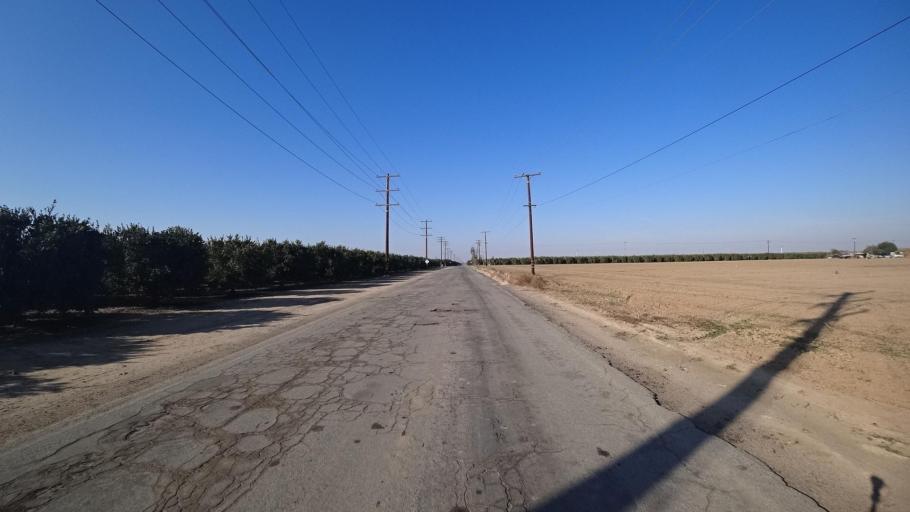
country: US
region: California
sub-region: Tulare County
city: Richgrove
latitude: 35.7327
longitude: -119.1323
